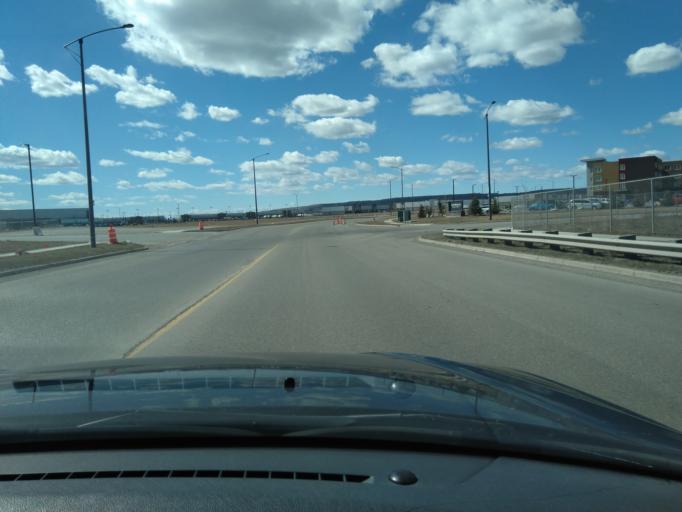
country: CA
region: Alberta
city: Calgary
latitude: 51.1373
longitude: -114.0253
